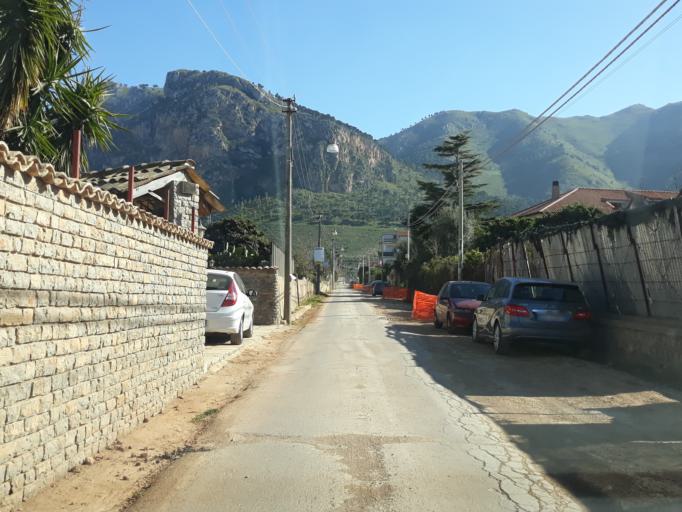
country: IT
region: Sicily
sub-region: Palermo
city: Villa Ciambra
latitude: 38.0817
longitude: 13.3462
